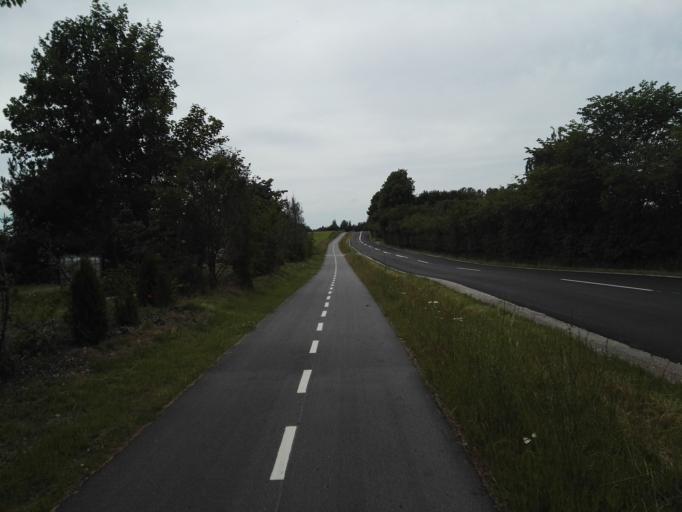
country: DK
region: Capital Region
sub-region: Hillerod Kommune
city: Skaevinge
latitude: 55.9170
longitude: 12.1897
